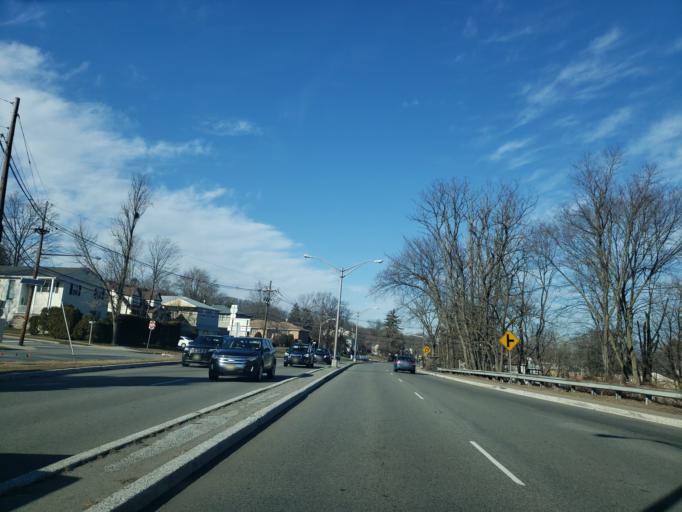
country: US
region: New Jersey
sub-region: Essex County
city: West Orange
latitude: 40.7997
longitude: -74.2655
